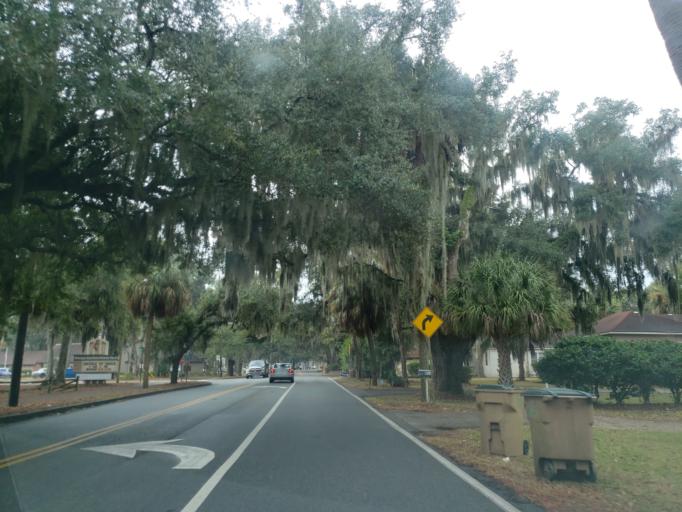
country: US
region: Georgia
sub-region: Chatham County
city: Wilmington Island
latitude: 32.0074
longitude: -80.9884
